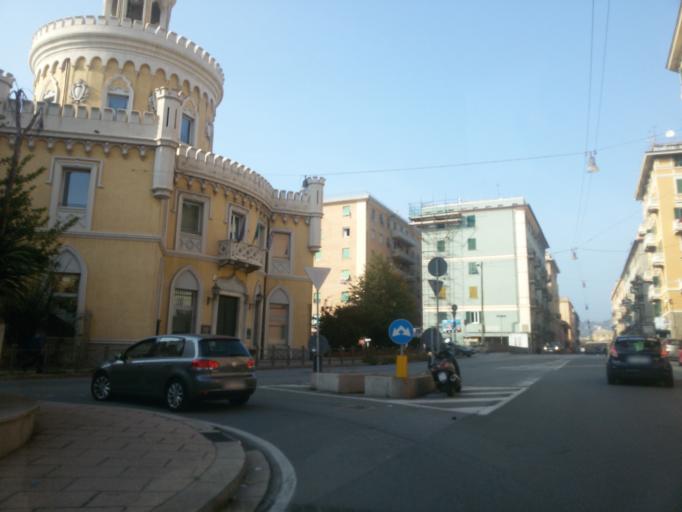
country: IT
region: Liguria
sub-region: Provincia di Genova
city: Genoa
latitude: 44.4341
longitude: 8.8929
